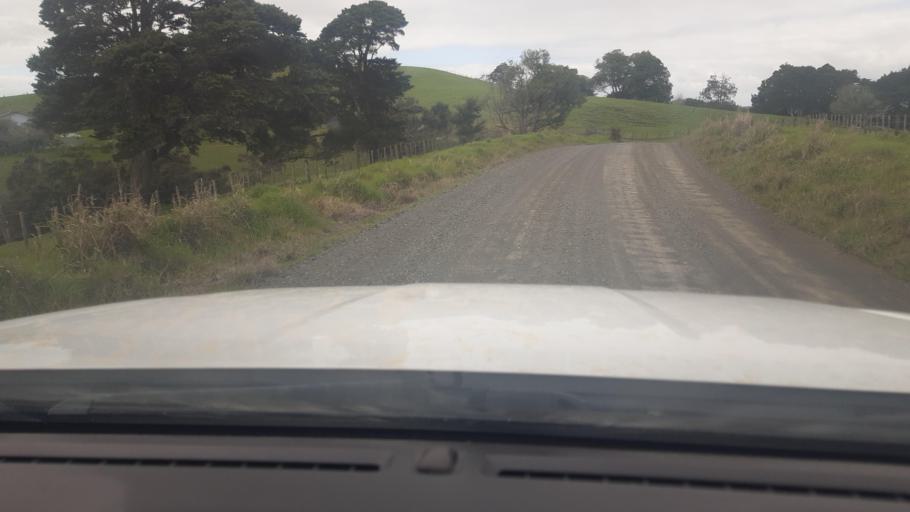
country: NZ
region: Northland
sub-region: Far North District
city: Kaitaia
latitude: -35.0909
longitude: 173.3168
